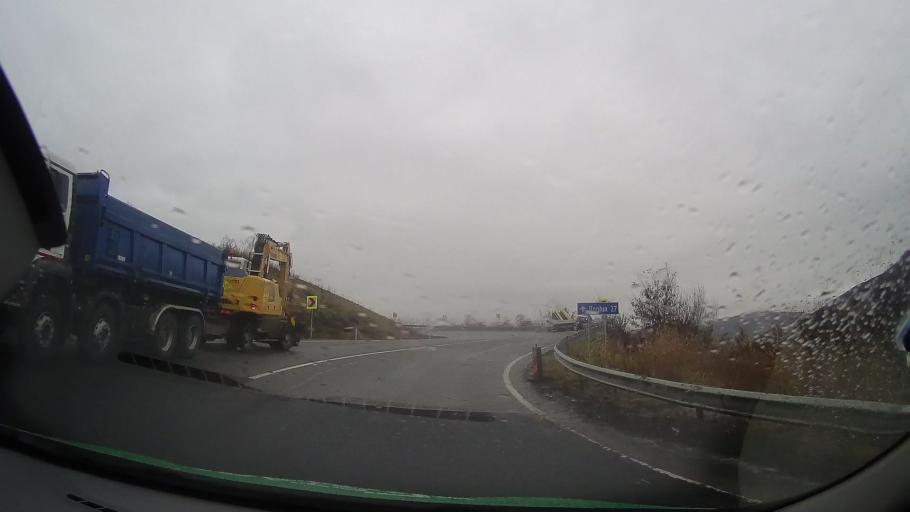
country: RO
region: Bistrita-Nasaud
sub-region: Comuna Teaca
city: Teaca
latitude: 46.9035
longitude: 24.4992
